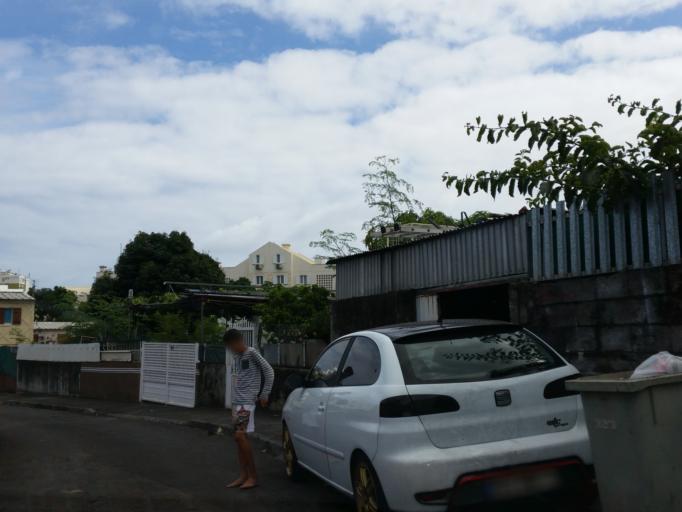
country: RE
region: Reunion
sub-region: Reunion
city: Saint-Denis
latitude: -20.8943
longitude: 55.4597
